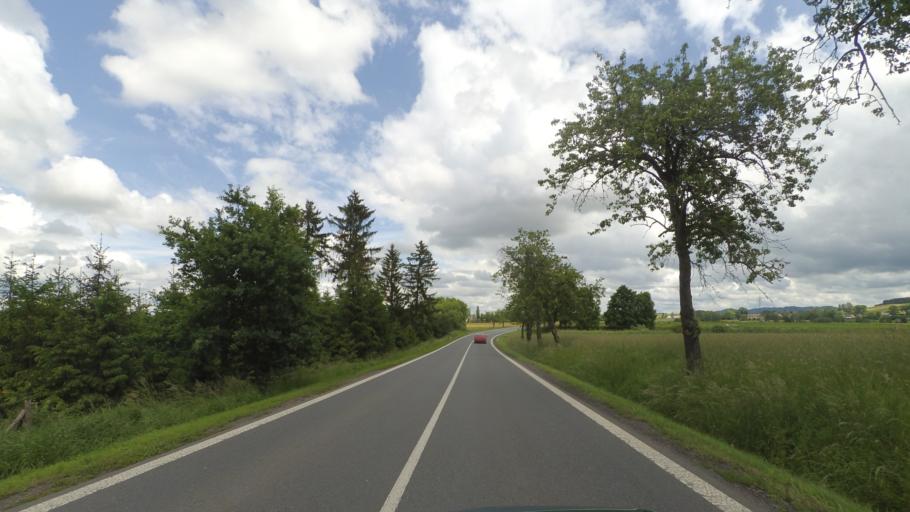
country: CZ
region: Plzensky
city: Janovice nad Uhlavou
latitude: 49.3713
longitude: 13.2538
